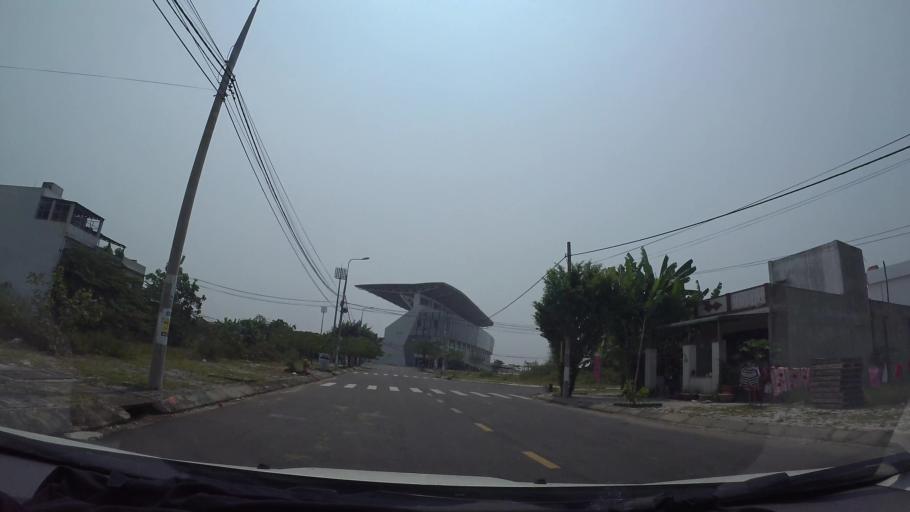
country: VN
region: Da Nang
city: Cam Le
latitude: 16.0008
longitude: 108.2218
